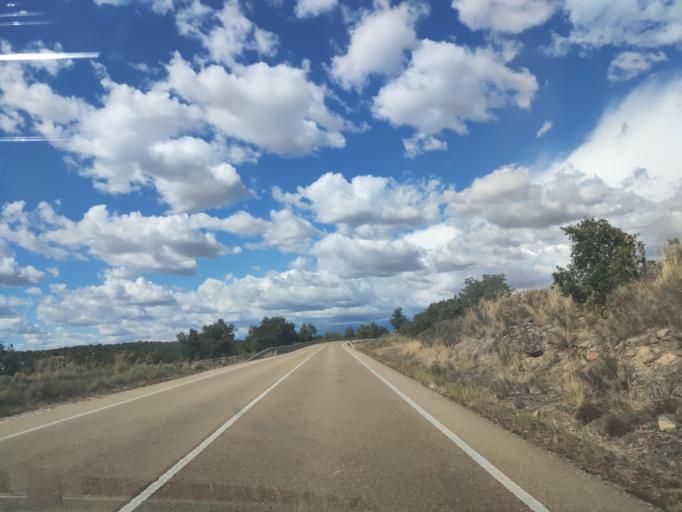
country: ES
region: Castille and Leon
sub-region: Provincia de Salamanca
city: Pozos de Hinojo
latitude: 40.9065
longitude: -6.3289
